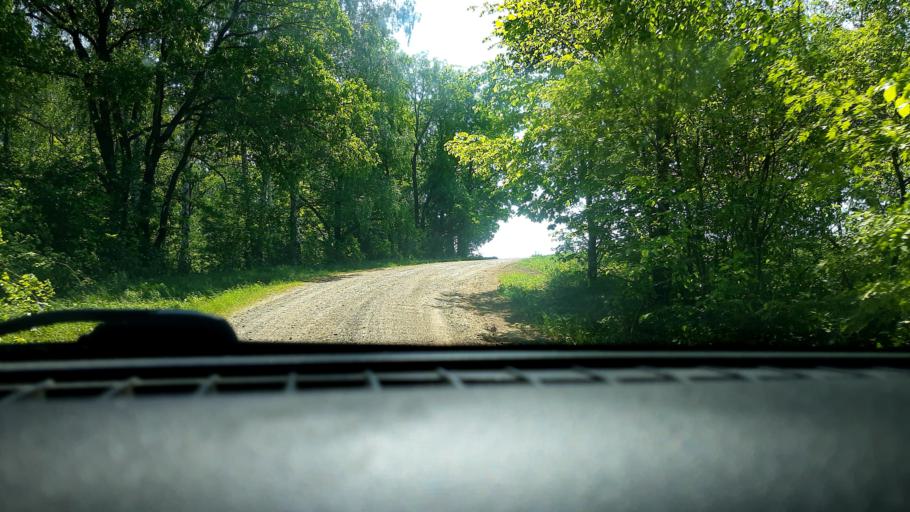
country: RU
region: Bashkortostan
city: Avdon
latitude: 54.4277
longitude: 55.8413
